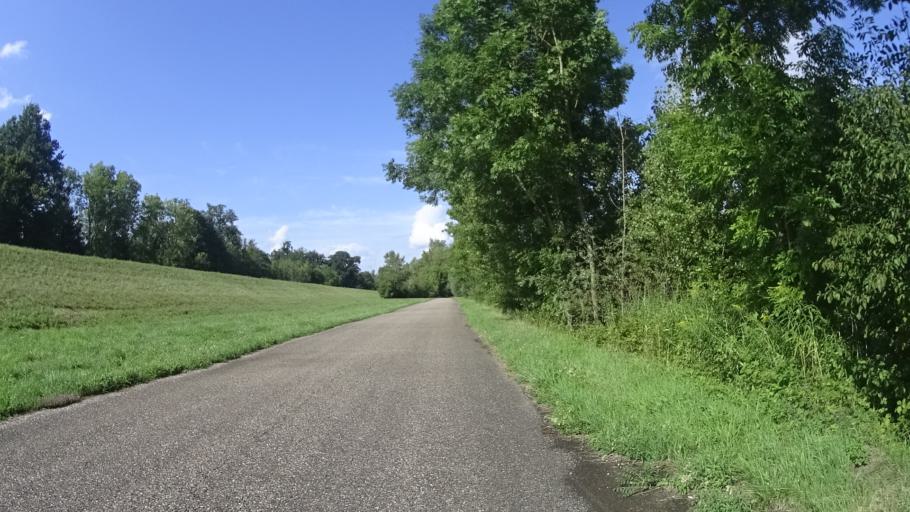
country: DE
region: Baden-Wuerttemberg
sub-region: Karlsruhe Region
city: Hugelsheim
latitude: 48.8362
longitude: 8.1022
